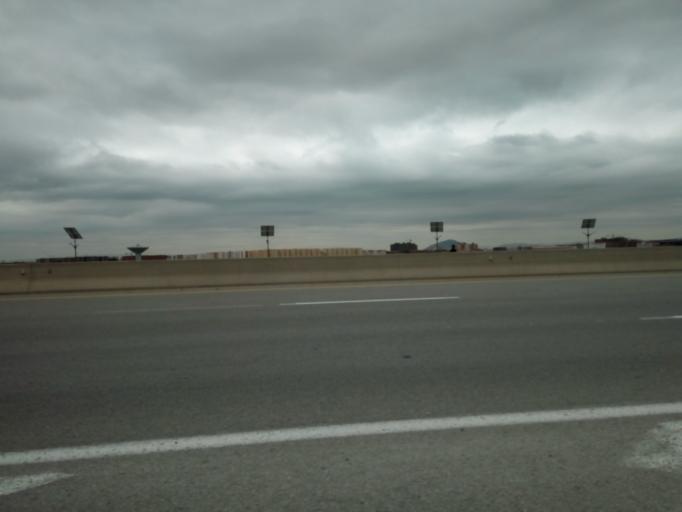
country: DZ
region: Setif
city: El Eulma
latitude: 36.1769
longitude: 5.6775
